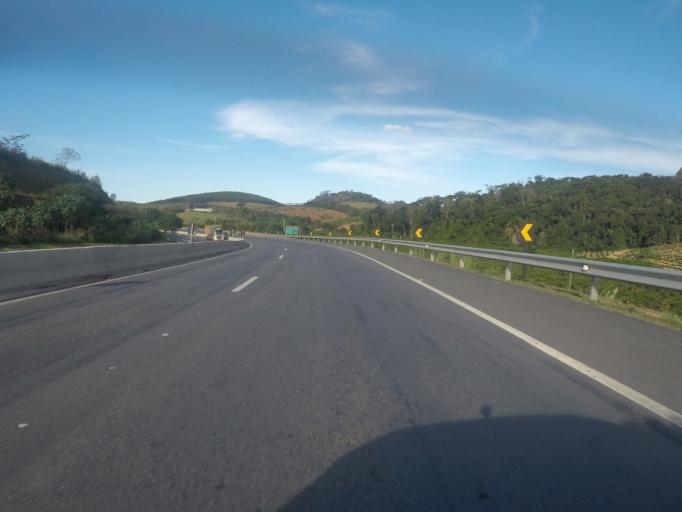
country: BR
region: Espirito Santo
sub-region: Ibiracu
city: Ibiracu
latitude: -19.8659
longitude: -40.3860
